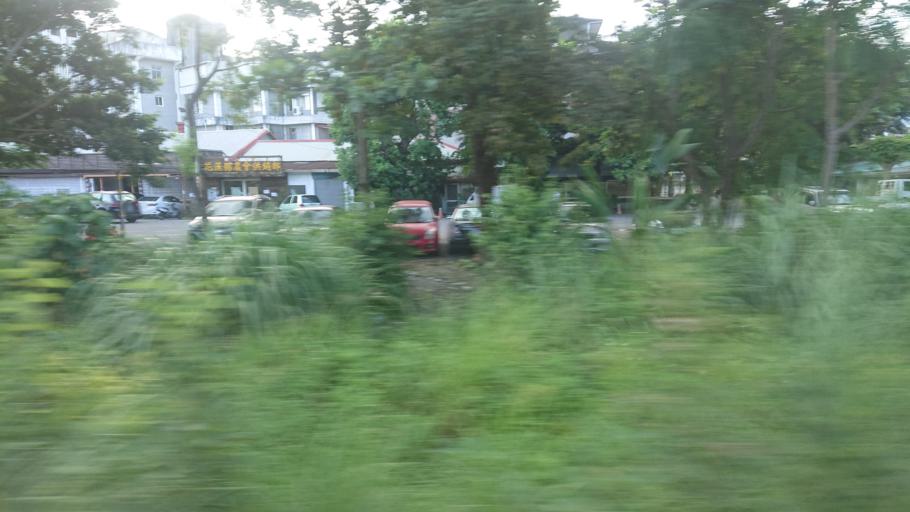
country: TW
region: Taiwan
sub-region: Hualien
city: Hualian
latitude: 23.9736
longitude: 121.5911
